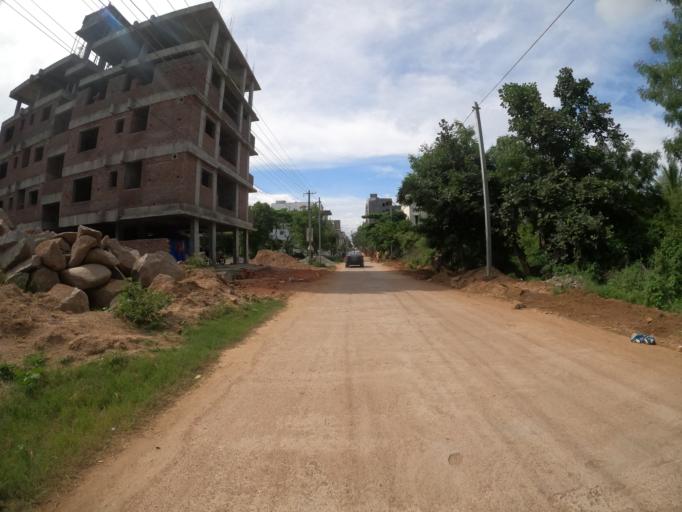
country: IN
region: Telangana
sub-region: Hyderabad
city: Hyderabad
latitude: 17.3554
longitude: 78.3948
